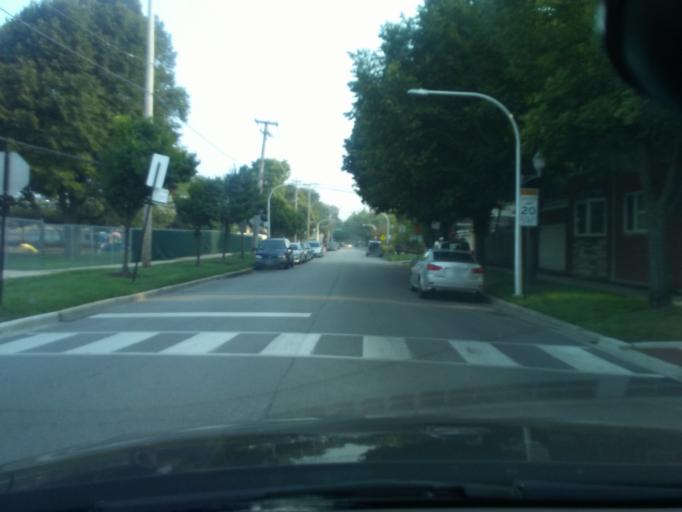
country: US
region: Illinois
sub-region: Cook County
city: Lincolnwood
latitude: 42.0102
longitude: -87.7045
